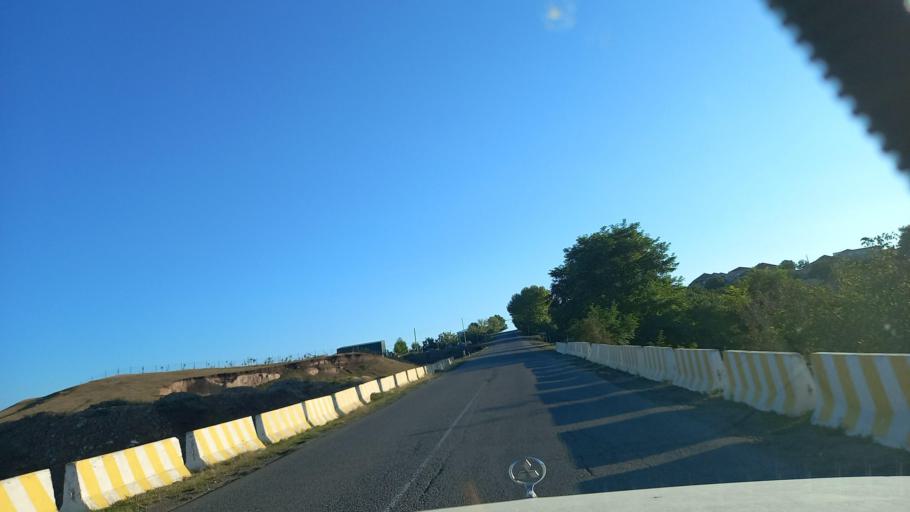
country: AZ
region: Shamkir Rayon
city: Shamkhor
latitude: 40.7738
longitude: 45.9594
